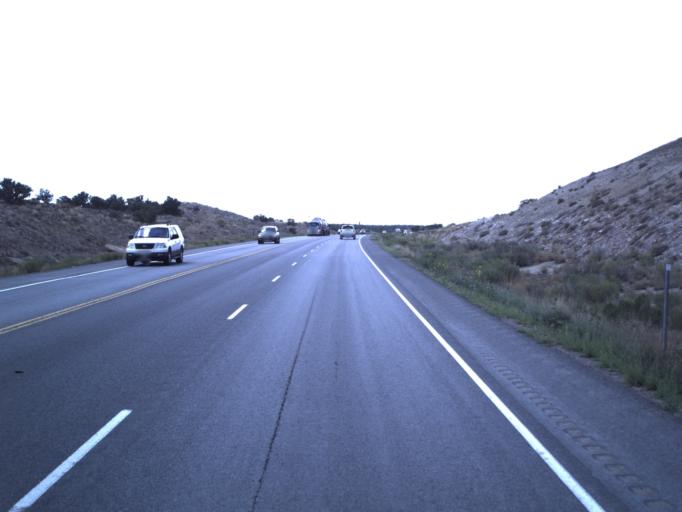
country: US
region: Utah
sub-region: Duchesne County
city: Duchesne
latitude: 40.1644
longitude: -110.4322
